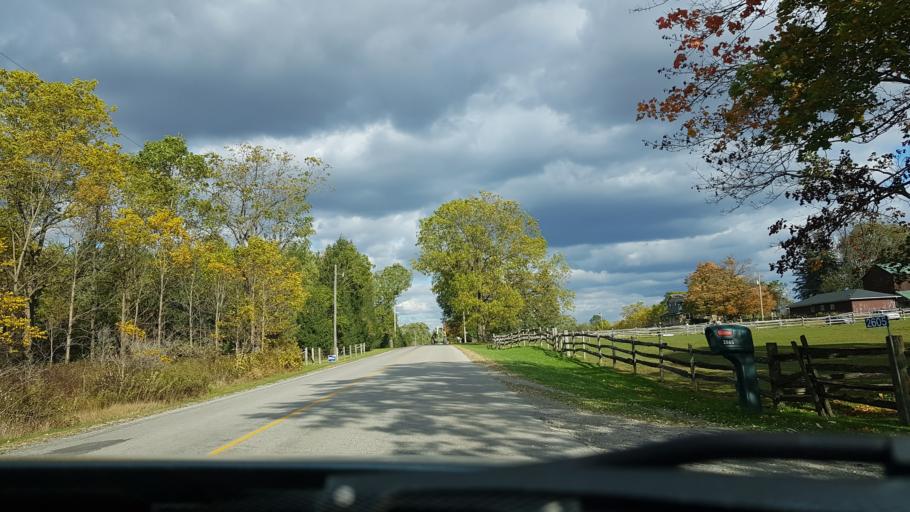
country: CA
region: Ontario
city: Delaware
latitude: 43.0101
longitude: -81.3848
